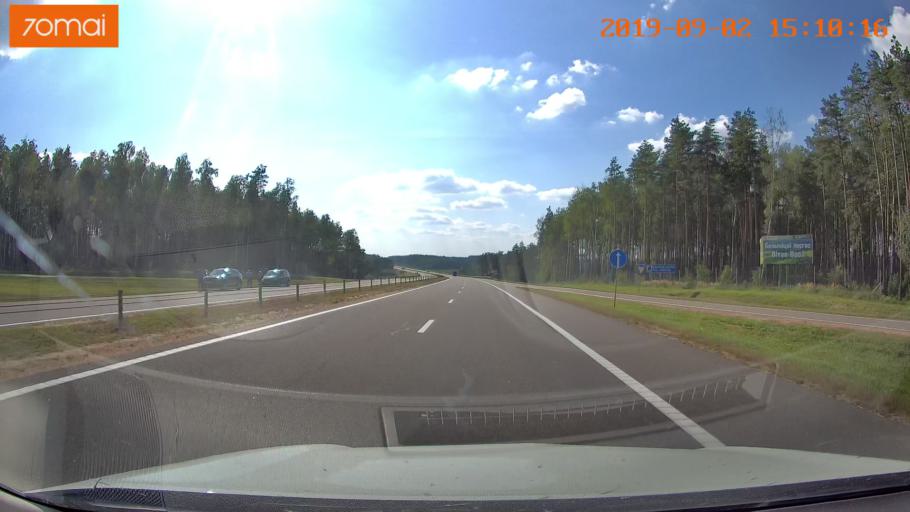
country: BY
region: Mogilev
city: Byalynichy
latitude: 53.9838
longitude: 29.7888
